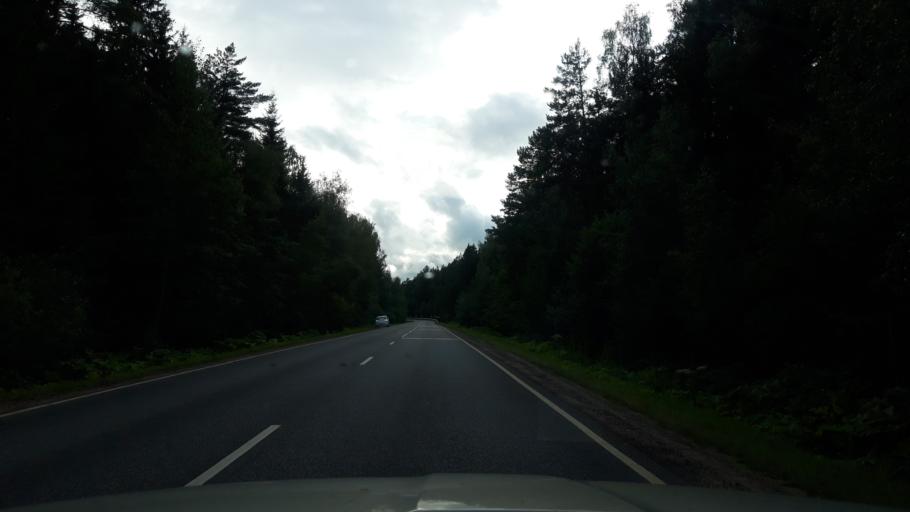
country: RU
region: Moskovskaya
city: Solnechnogorsk
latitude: 56.0956
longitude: 36.8820
